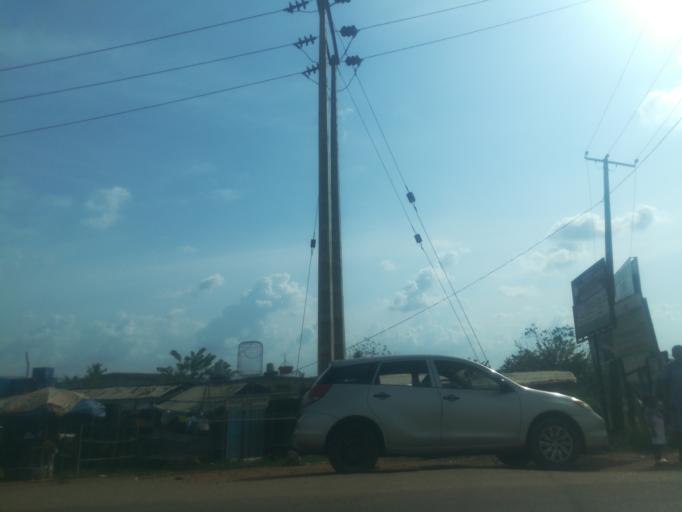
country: NG
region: Oyo
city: Ibadan
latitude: 7.3908
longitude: 3.8165
